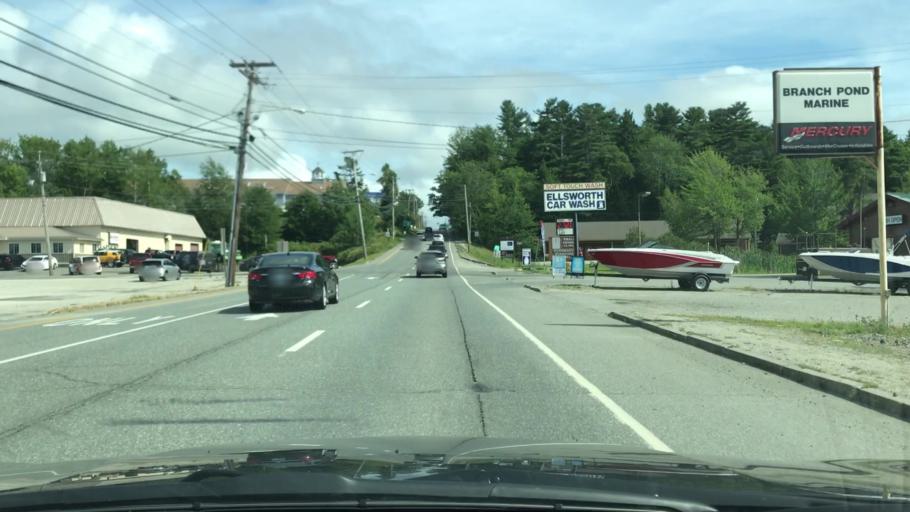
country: US
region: Maine
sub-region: Hancock County
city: Ellsworth
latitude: 44.5303
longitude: -68.4054
